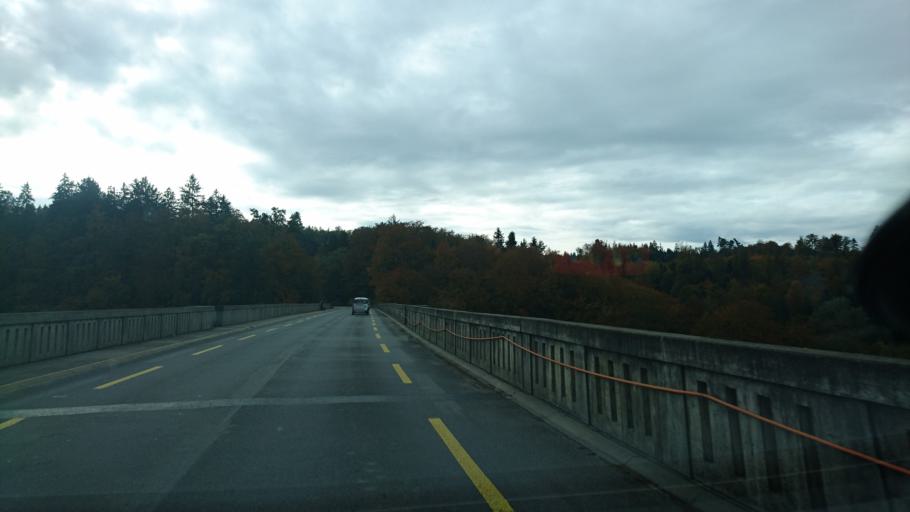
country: CH
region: Bern
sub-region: Bern-Mittelland District
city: Kirchlindach
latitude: 46.9720
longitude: 7.4181
